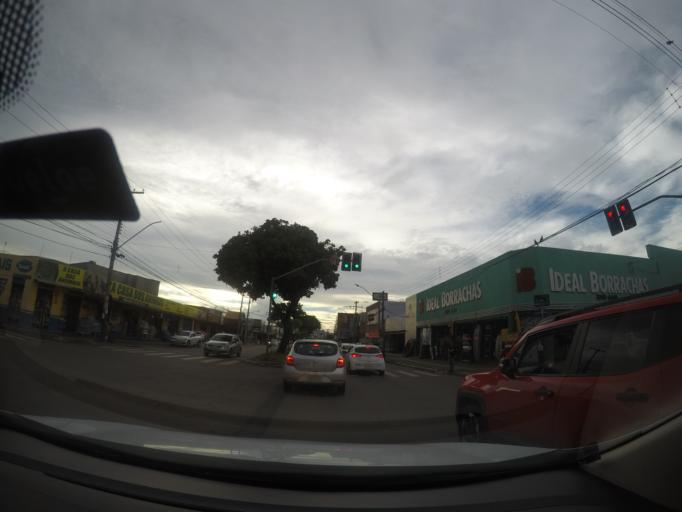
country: BR
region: Goias
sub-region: Goiania
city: Goiania
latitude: -16.6751
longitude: -49.2931
